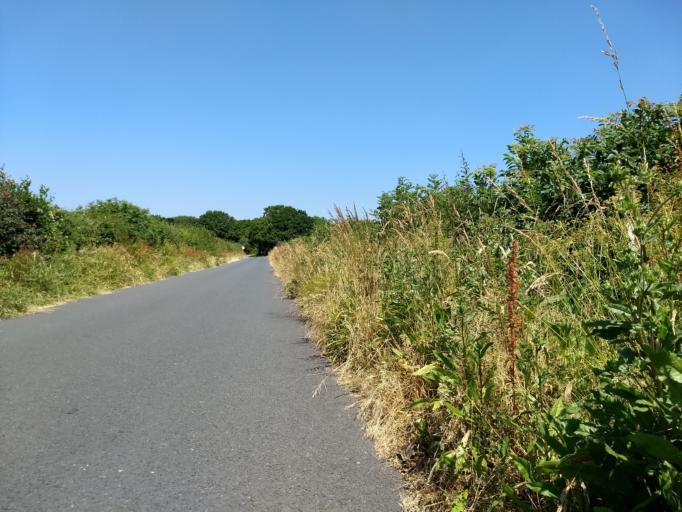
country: GB
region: England
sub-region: Isle of Wight
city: Shalfleet
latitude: 50.7112
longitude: -1.3612
